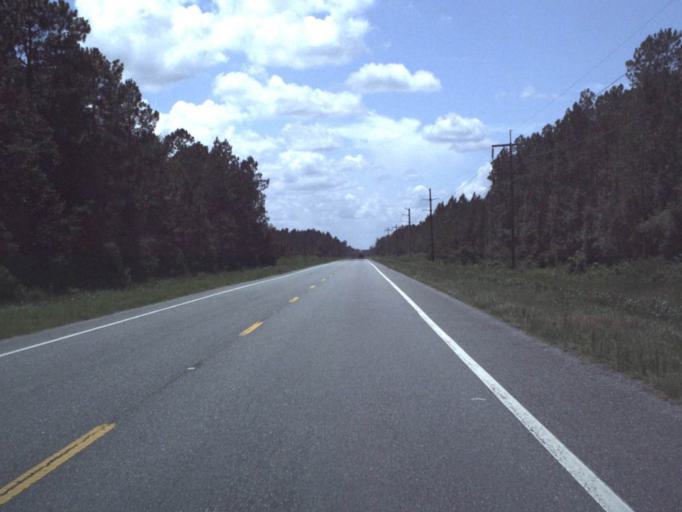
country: US
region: Florida
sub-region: Bradford County
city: Starke
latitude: 29.9754
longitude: -82.2223
